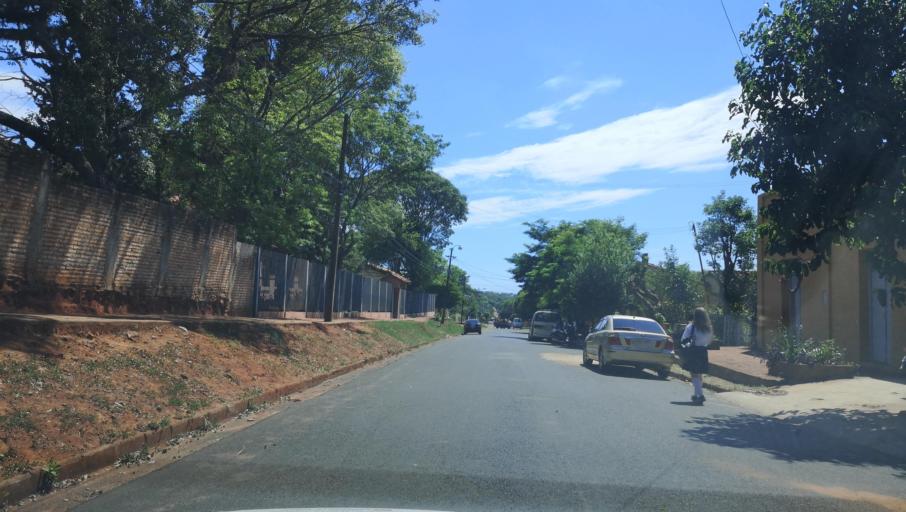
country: PY
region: Misiones
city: Santa Maria
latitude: -26.8901
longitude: -57.0293
